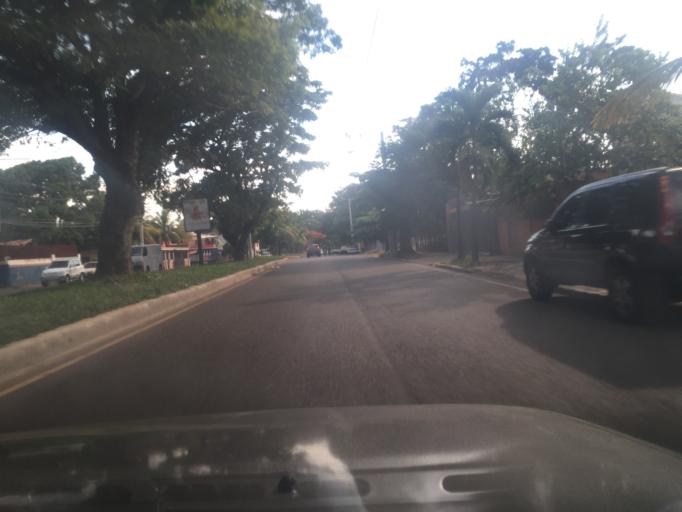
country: DO
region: Santiago
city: Santiago de los Caballeros
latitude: 19.4401
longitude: -70.7181
